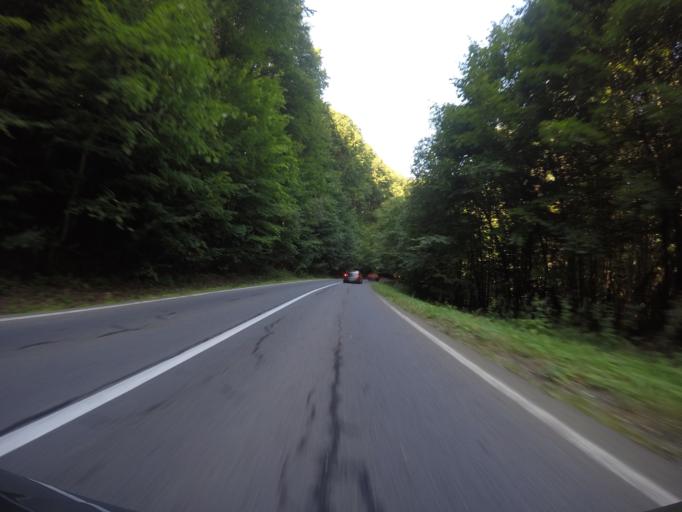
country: RO
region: Brasov
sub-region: Comuna Cristian
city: Cristian
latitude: 45.5822
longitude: 25.5099
